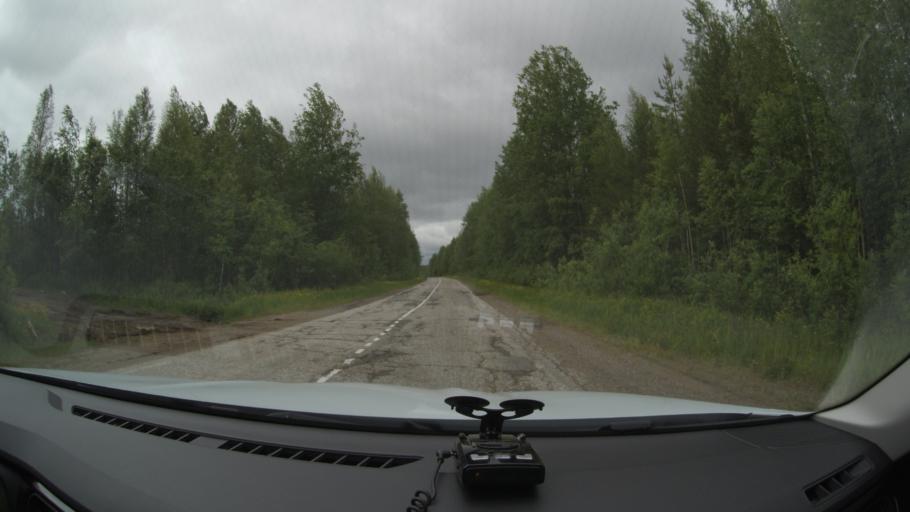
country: RU
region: Komi Republic
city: Nizhniy Odes
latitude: 63.6054
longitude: 54.5062
